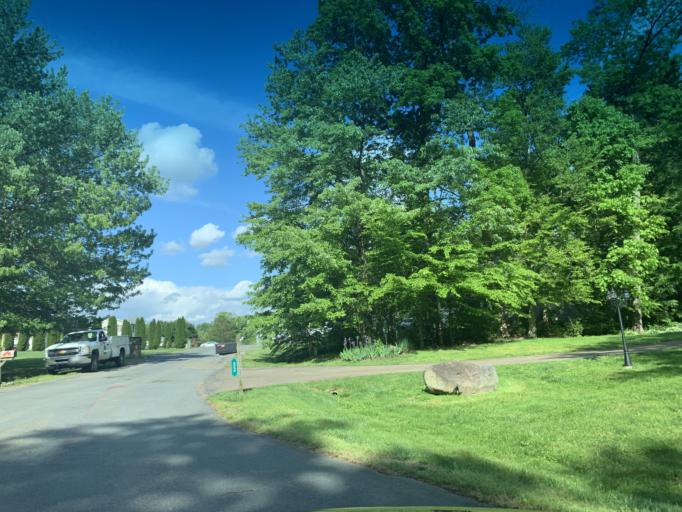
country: US
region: Maryland
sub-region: Cecil County
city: Rising Sun
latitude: 39.6944
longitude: -76.1463
